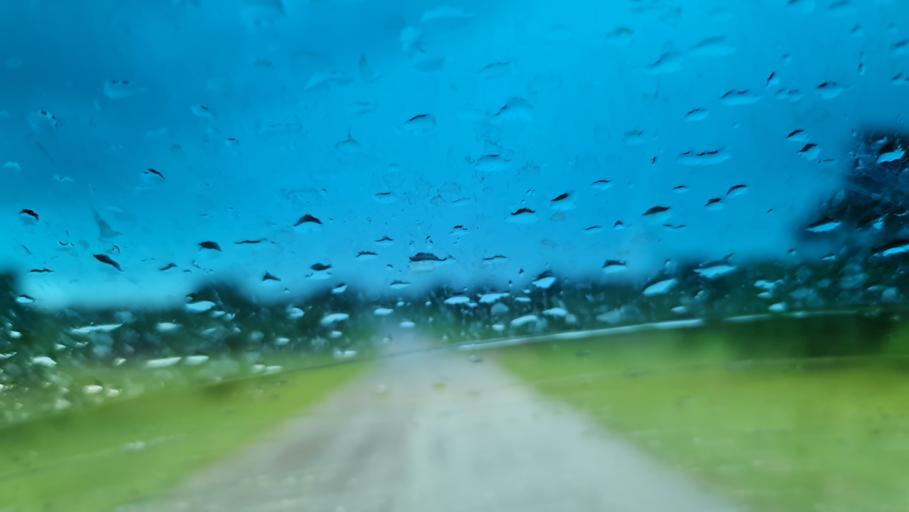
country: MZ
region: Nampula
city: Antonio Enes
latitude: -15.9292
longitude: 39.4809
